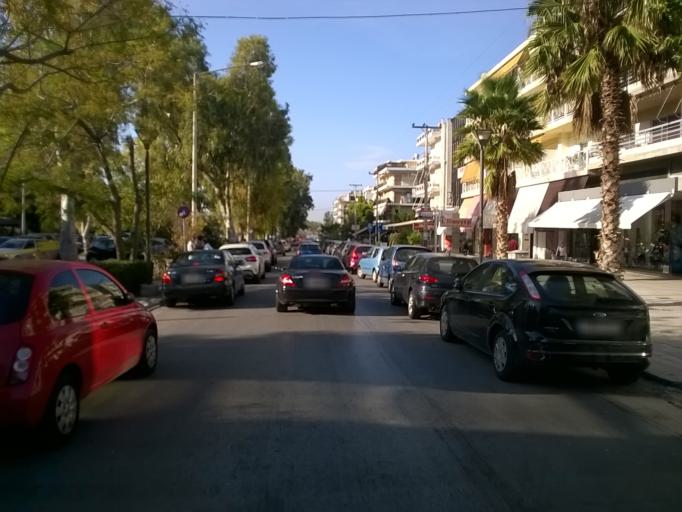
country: GR
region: Attica
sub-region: Nomarchia Athinas
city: Glyfada
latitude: 37.8621
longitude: 23.7519
